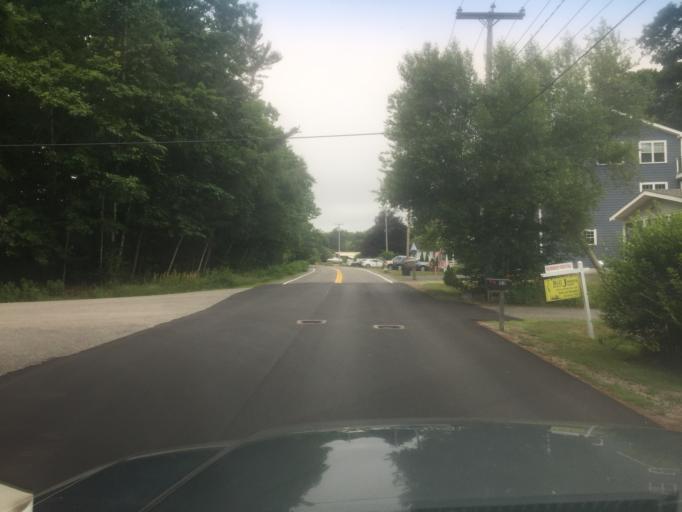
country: US
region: Maine
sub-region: York County
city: York Beach
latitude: 43.1581
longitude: -70.6268
